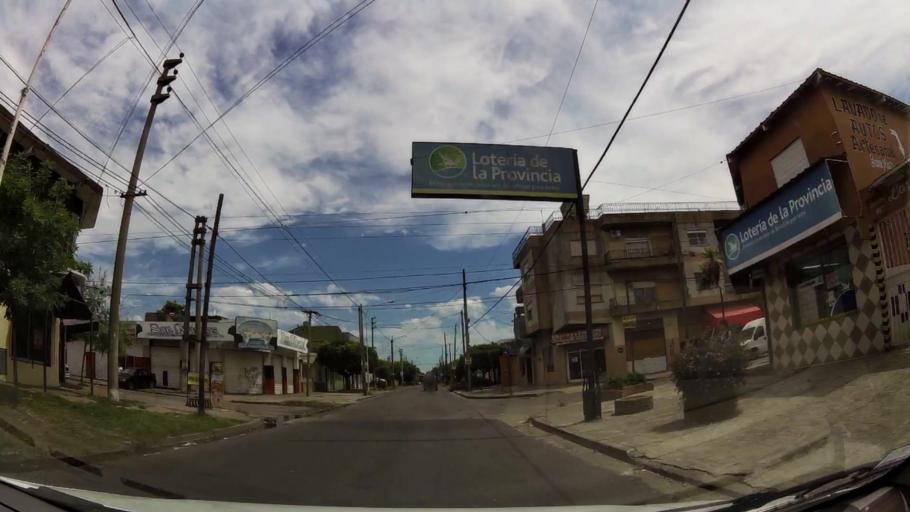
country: AR
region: Buenos Aires
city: San Justo
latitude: -34.6846
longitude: -58.5280
